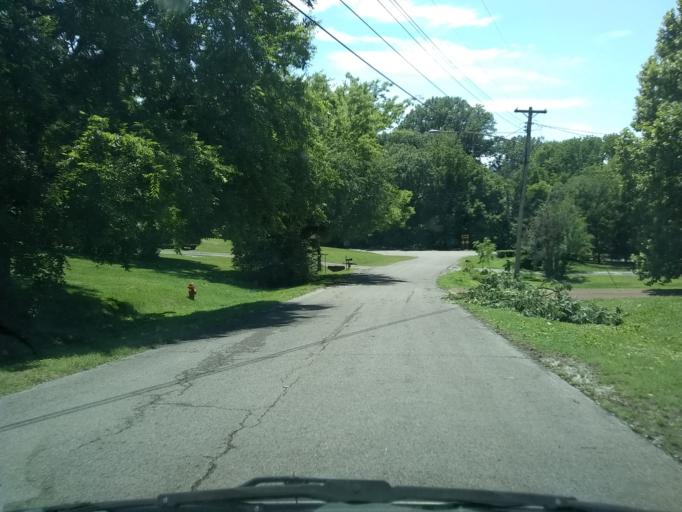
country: US
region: Tennessee
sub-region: Davidson County
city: Nashville
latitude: 36.1330
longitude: -86.7079
